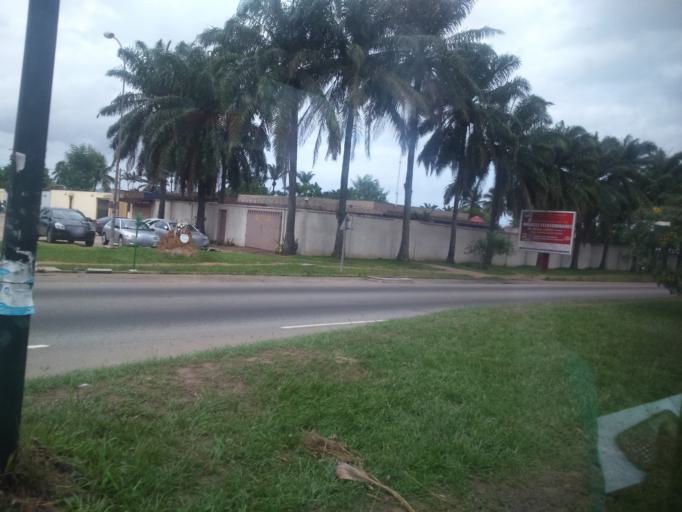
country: CI
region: Lagunes
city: Abidjan
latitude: 5.3595
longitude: -3.9994
